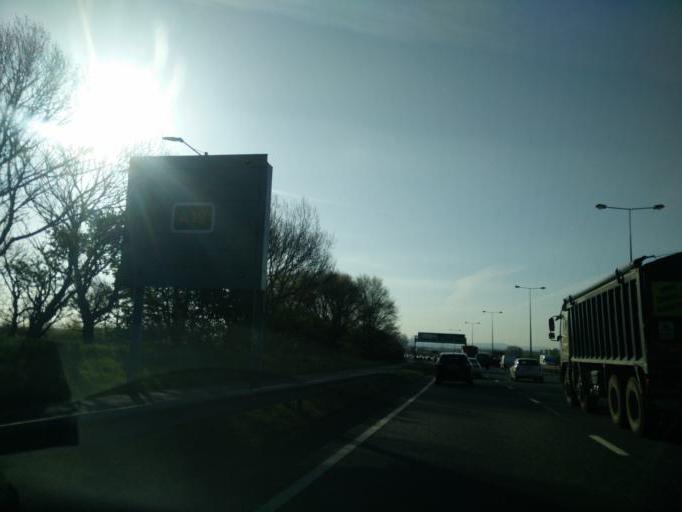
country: GB
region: England
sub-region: Stockton-on-Tees
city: Billingham
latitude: 54.5824
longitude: -1.2946
